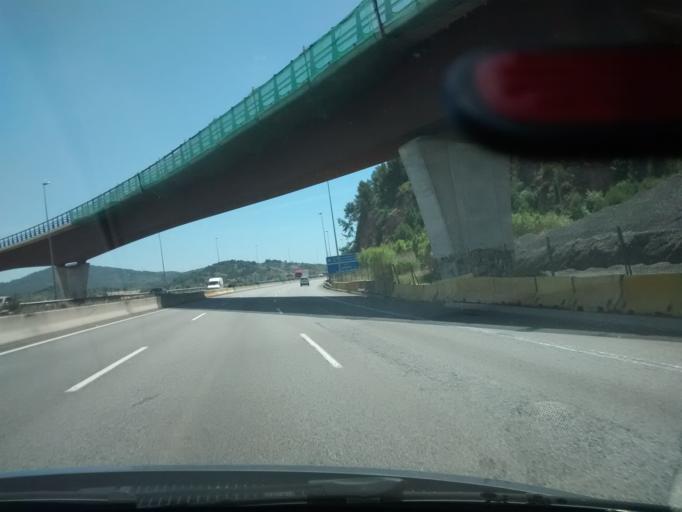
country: ES
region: Catalonia
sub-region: Provincia de Barcelona
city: Palleja
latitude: 41.4389
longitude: 1.9901
